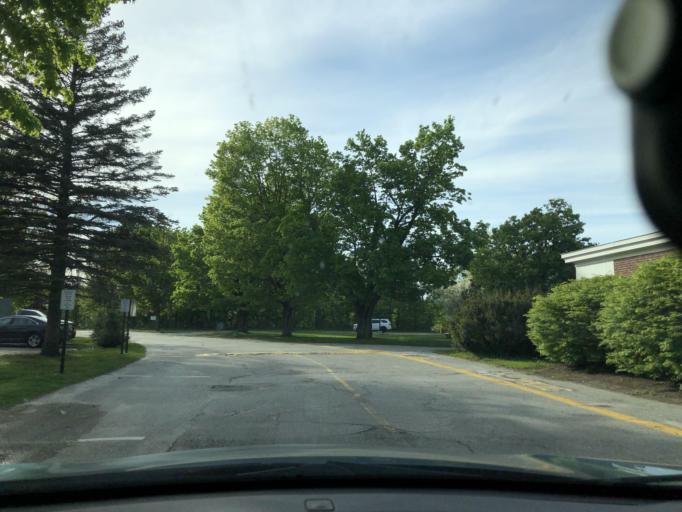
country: US
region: New Hampshire
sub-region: Merrimack County
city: New London
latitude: 43.4169
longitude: -71.9874
